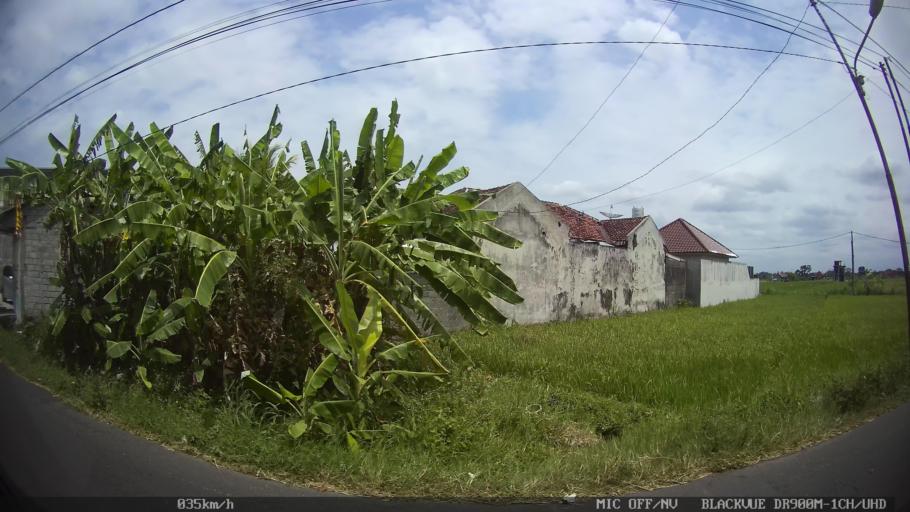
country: ID
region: Central Java
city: Candi Prambanan
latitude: -7.7846
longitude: 110.4789
